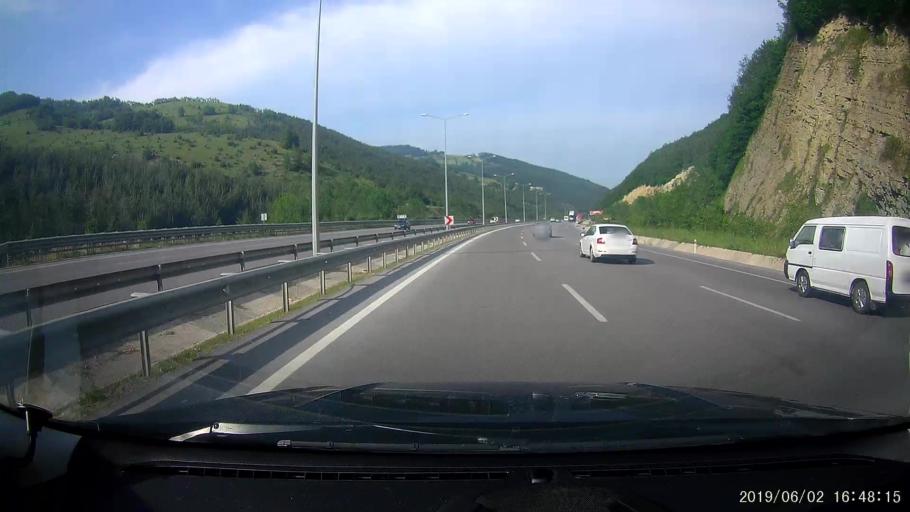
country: TR
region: Samsun
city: Kavak
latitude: 41.2247
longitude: 36.1312
